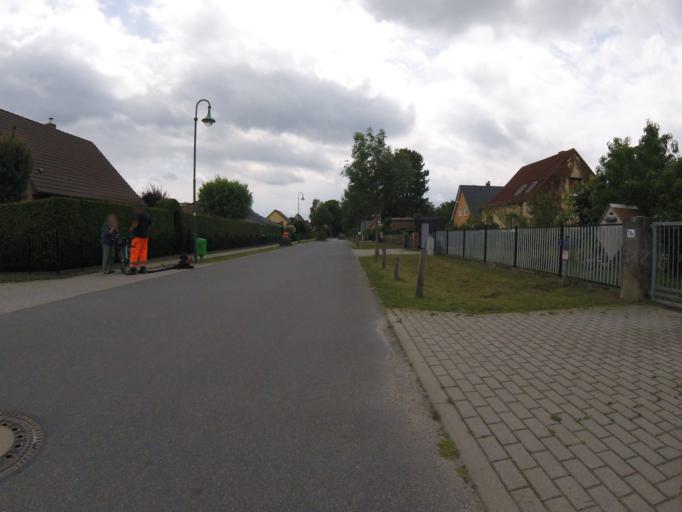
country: DE
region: Brandenburg
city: Konigs Wusterhausen
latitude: 52.2816
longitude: 13.6404
